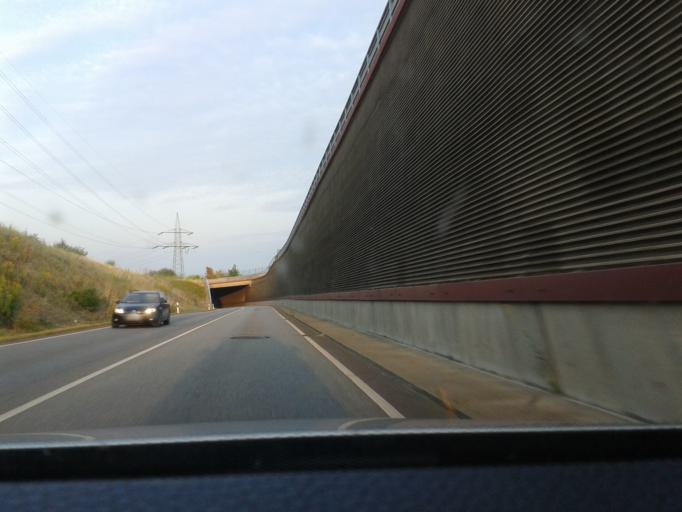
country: DE
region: Saxony
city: Kreischa
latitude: 50.9950
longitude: 13.7803
